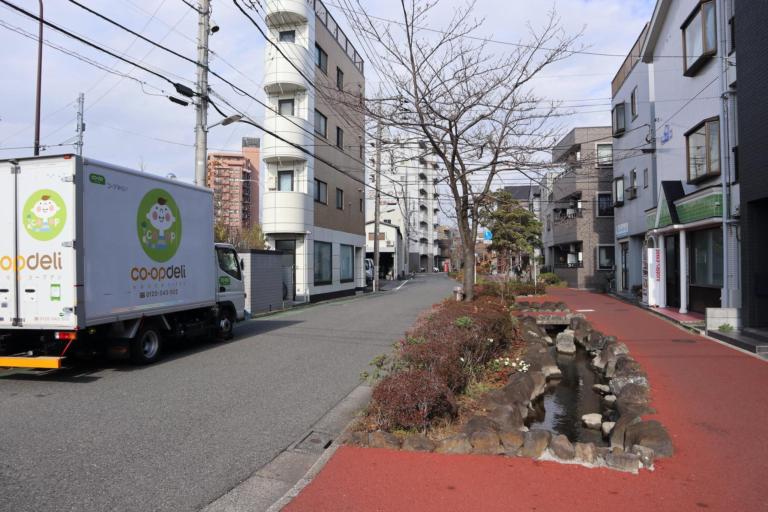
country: JP
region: Tokyo
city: Urayasu
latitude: 35.6882
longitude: 139.8833
